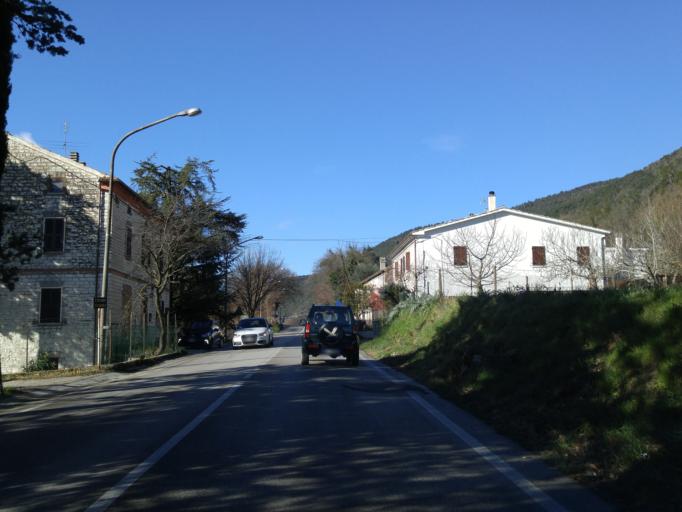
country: IT
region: The Marches
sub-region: Provincia di Pesaro e Urbino
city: Fossombrone
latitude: 43.6862
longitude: 12.7938
